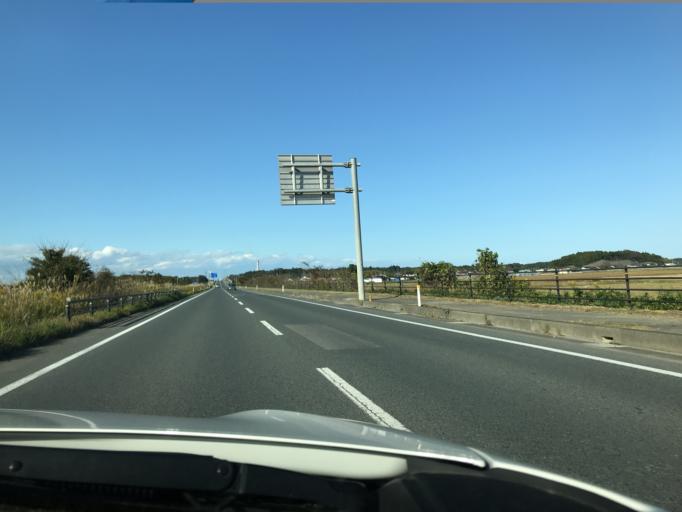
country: JP
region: Miyagi
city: Marumori
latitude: 37.7961
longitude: 140.9439
